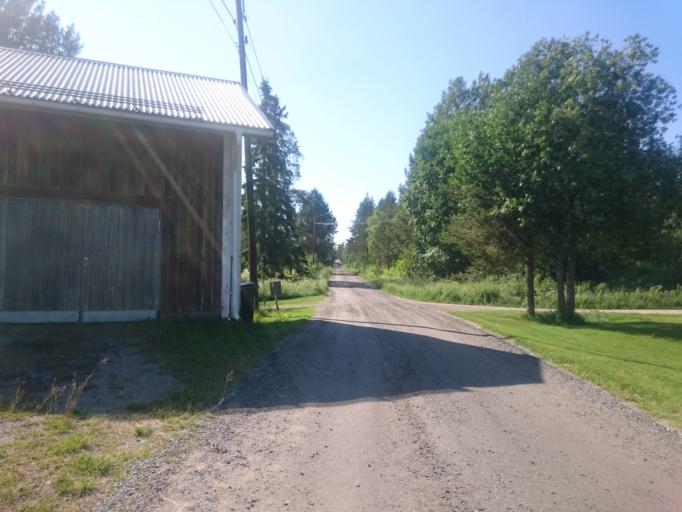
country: SE
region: Vaesternorrland
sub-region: OErnskoeldsviks Kommun
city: Bredbyn
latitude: 63.3003
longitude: 18.2657
